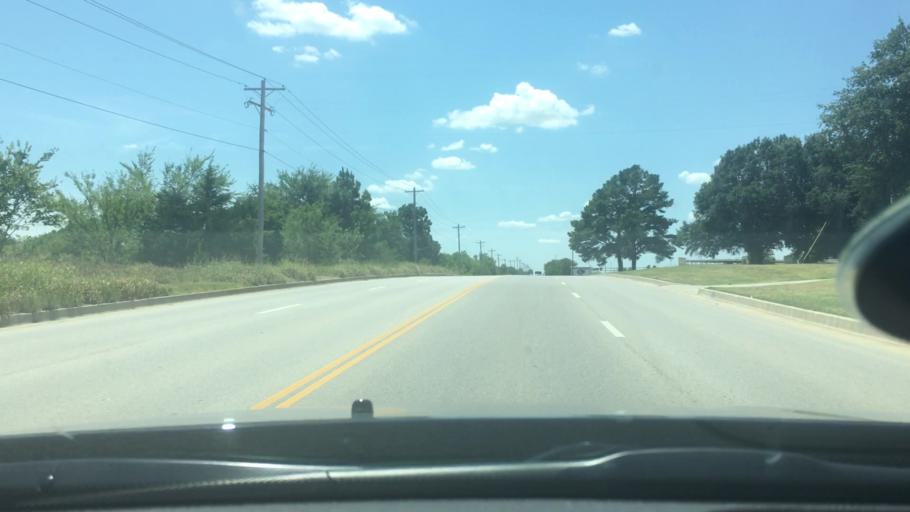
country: US
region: Oklahoma
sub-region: Bryan County
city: Calera
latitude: 33.9586
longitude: -96.4021
